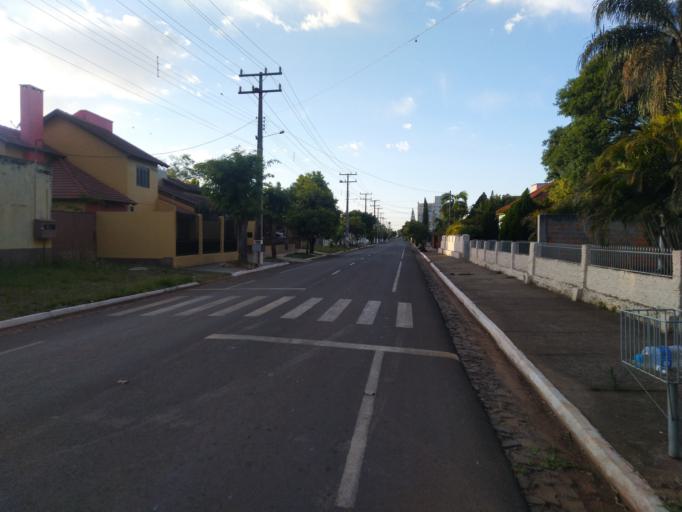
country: BR
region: Rio Grande do Sul
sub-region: Sao Borja
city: Sao Borja
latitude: -28.6518
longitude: -56.0107
